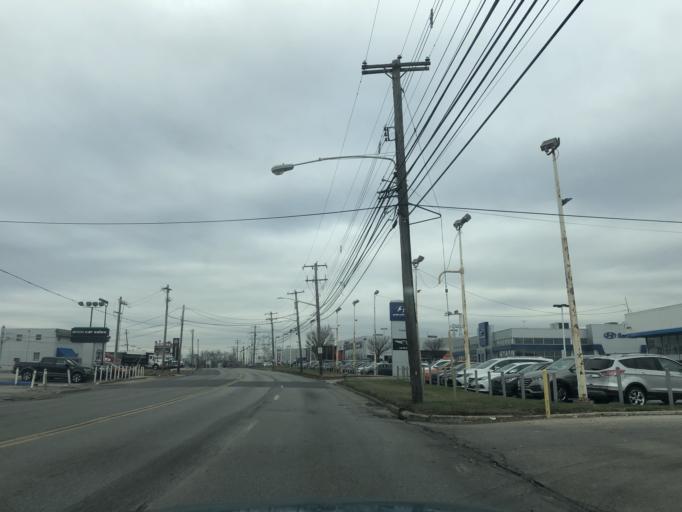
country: US
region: Pennsylvania
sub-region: Montgomery County
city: Conshohocken
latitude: 40.1020
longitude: -75.3065
